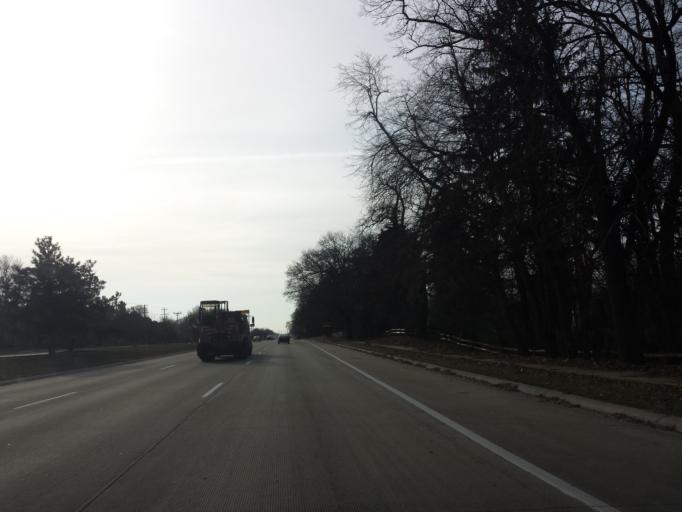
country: US
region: Michigan
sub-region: Oakland County
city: Franklin
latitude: 42.5511
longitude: -83.2854
